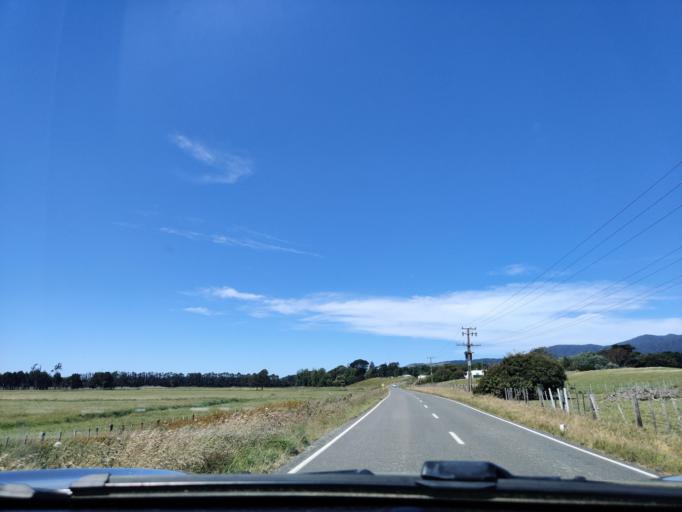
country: NZ
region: Wellington
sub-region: Upper Hutt City
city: Upper Hutt
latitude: -41.3275
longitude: 175.2225
